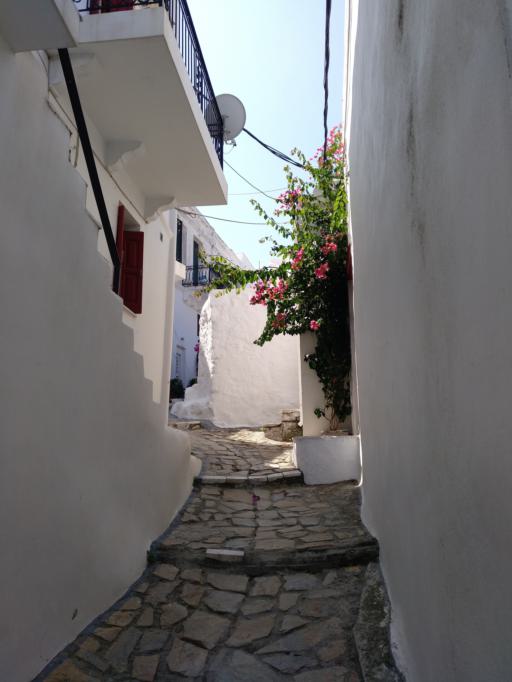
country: GR
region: Central Greece
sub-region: Nomos Evvoias
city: Skyros
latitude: 38.9072
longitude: 24.5667
